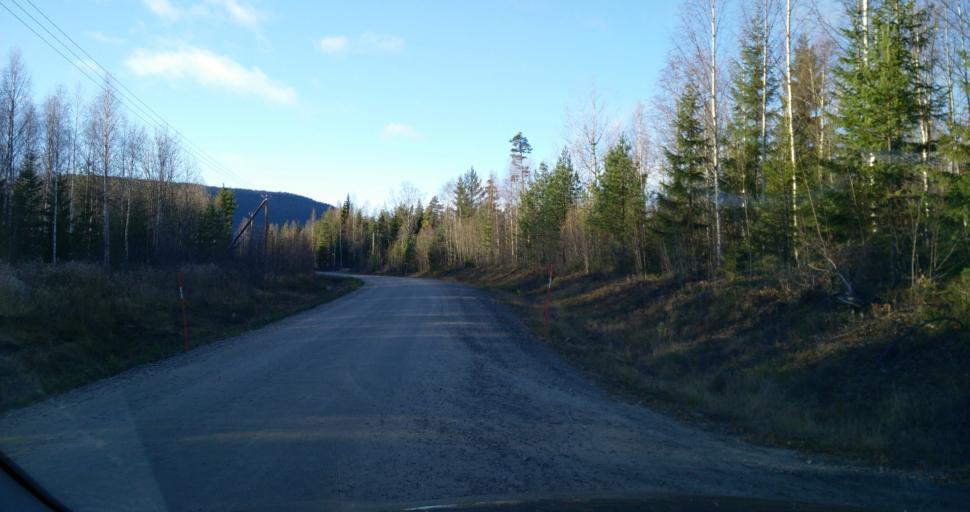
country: SE
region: Gaevleborg
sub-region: Nordanstigs Kommun
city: Bergsjoe
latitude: 62.0580
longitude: 16.8095
